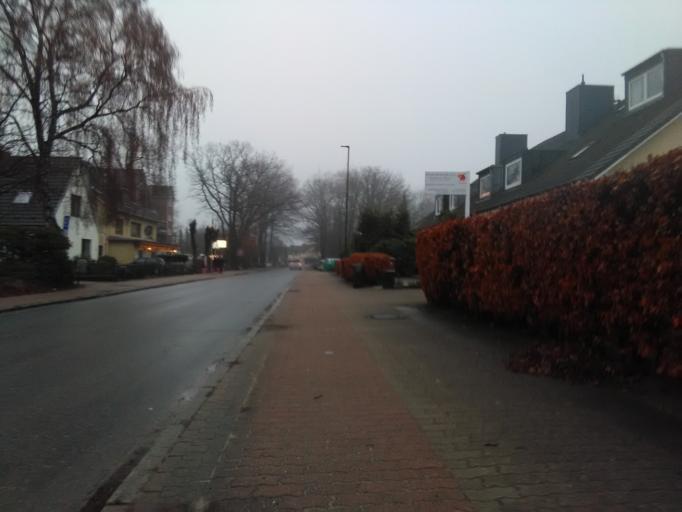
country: DE
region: Schleswig-Holstein
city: Quickborn
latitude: 53.7267
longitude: 9.9147
